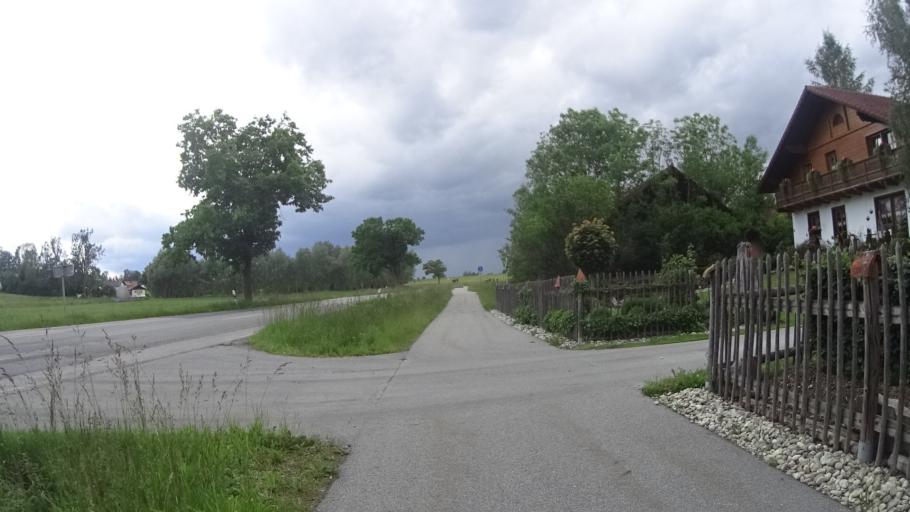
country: DE
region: Bavaria
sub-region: Upper Bavaria
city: Egglkofen
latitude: 48.4479
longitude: 12.4827
